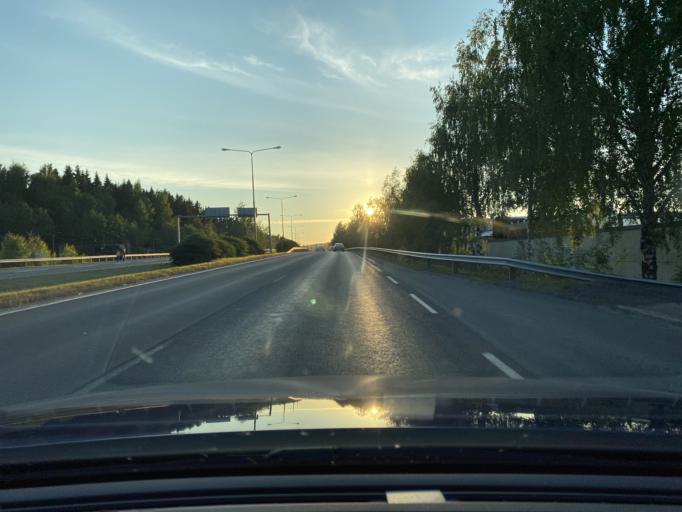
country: FI
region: Pirkanmaa
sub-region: Tampere
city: Pirkkala
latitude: 61.5155
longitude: 23.6610
